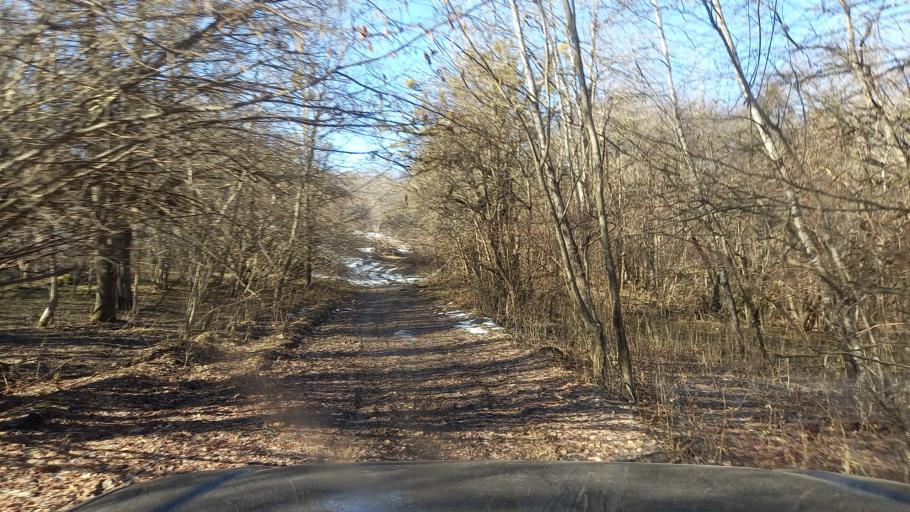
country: RU
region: Adygeya
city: Kamennomostskiy
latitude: 44.2796
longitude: 40.3278
